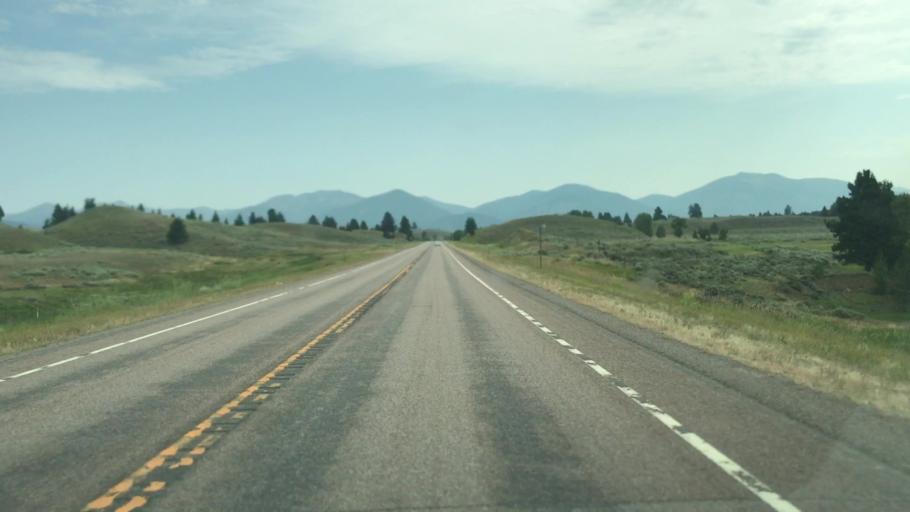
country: US
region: Montana
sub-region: Missoula County
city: Seeley Lake
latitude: 47.0312
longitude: -113.2368
